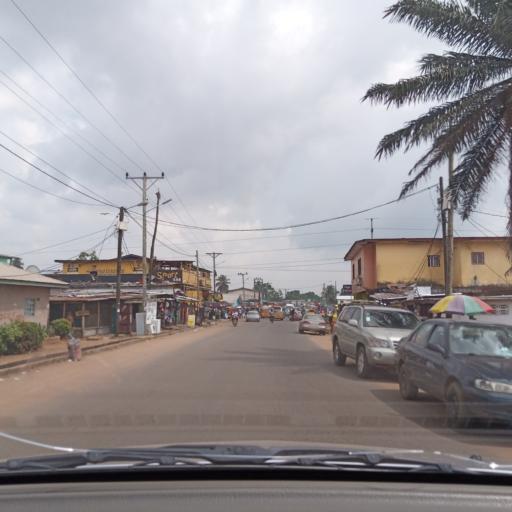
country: LR
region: Montserrado
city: Monrovia
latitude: 6.2747
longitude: -10.6934
